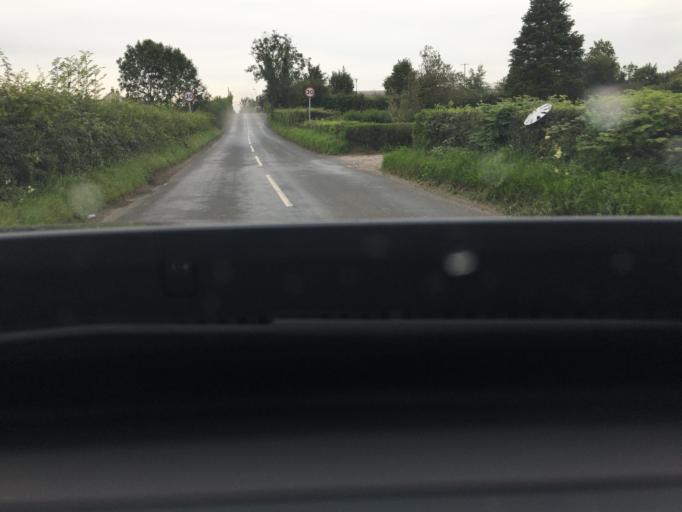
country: GB
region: Northern Ireland
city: Coalisland
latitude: 54.5365
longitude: -6.6177
